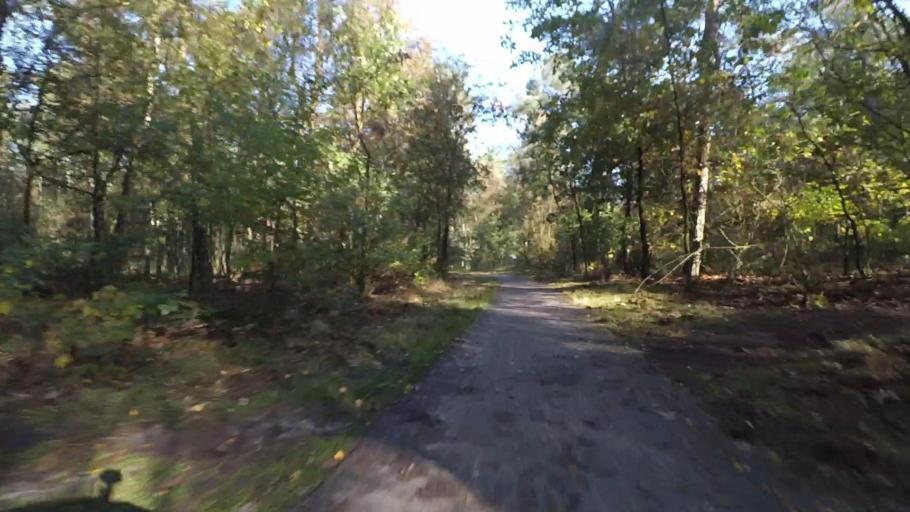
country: NL
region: Gelderland
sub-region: Gemeente Ermelo
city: Ermelo
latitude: 52.3134
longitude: 5.6455
